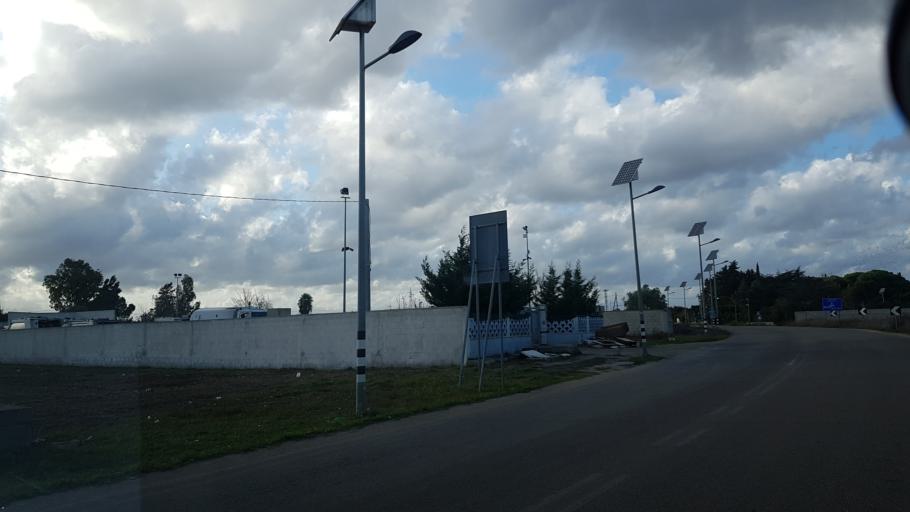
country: IT
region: Apulia
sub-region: Provincia di Brindisi
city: San Pietro Vernotico
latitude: 40.4982
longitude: 18.0057
